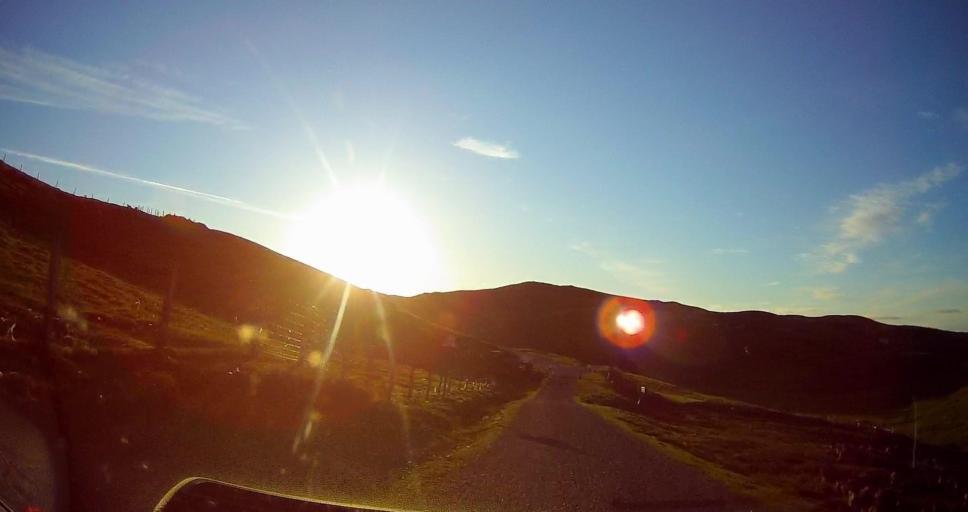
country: GB
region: Scotland
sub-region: Shetland Islands
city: Lerwick
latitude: 60.4476
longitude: -1.4154
